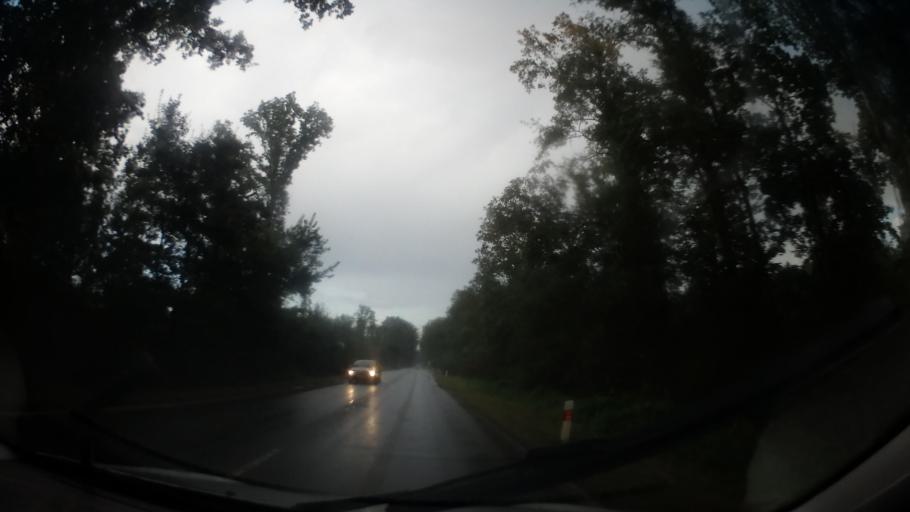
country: CZ
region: Olomoucky
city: Cervenka
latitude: 49.7139
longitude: 17.1295
